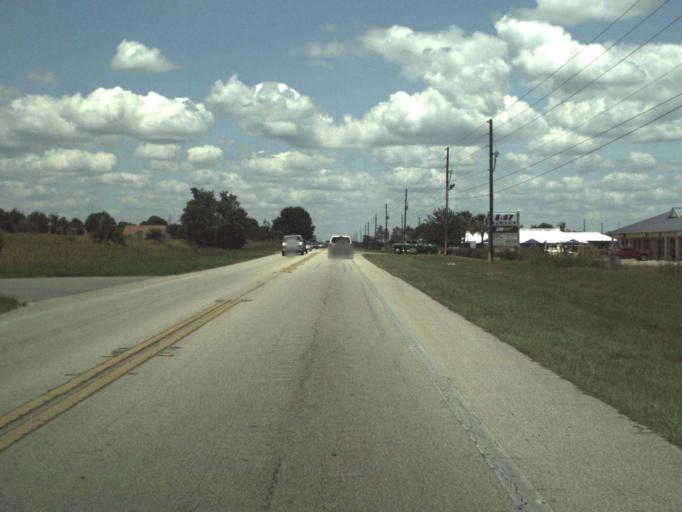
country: US
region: Florida
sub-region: Marion County
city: Silver Springs Shores
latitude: 29.0947
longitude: -82.0535
